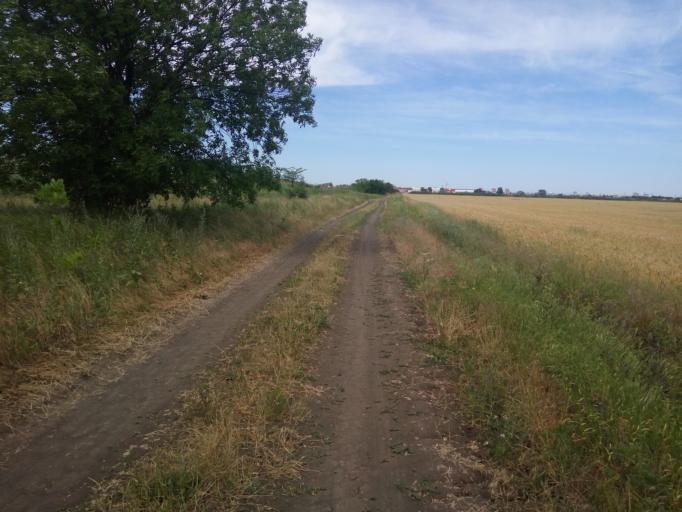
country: RU
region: Rostov
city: Bataysk
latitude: 47.1157
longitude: 39.7227
